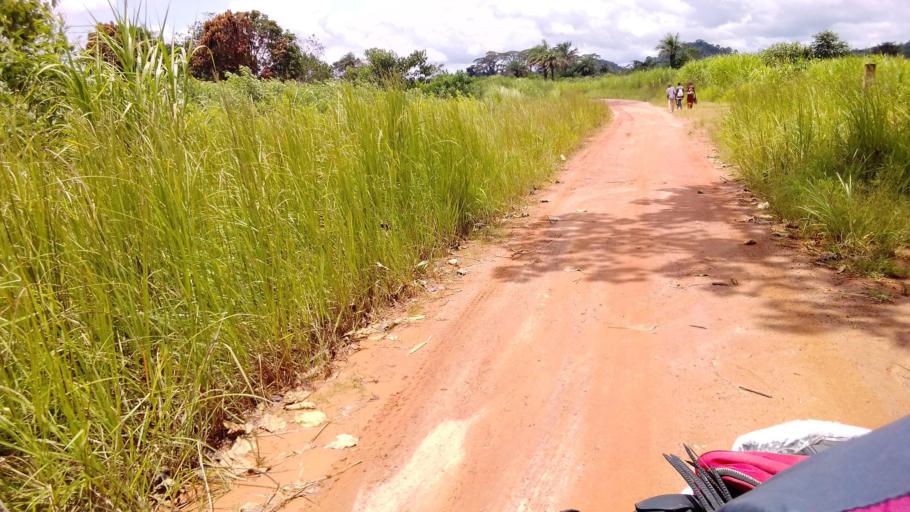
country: SL
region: Eastern Province
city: Koidu
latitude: 8.6717
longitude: -10.9544
